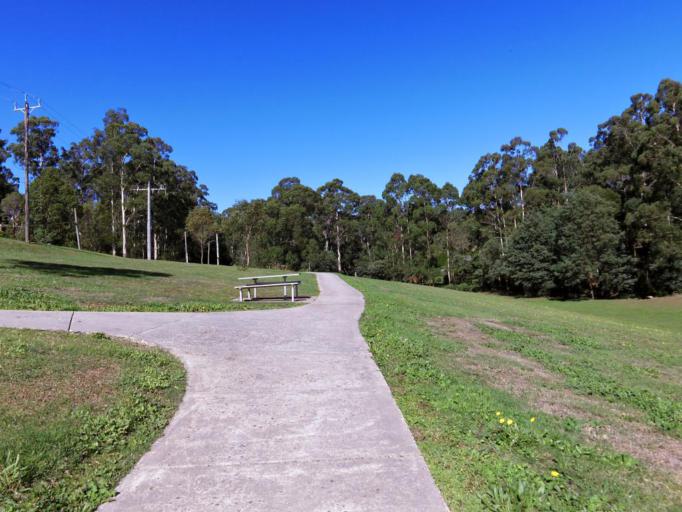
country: AU
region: Victoria
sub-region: Cardinia
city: Cockatoo
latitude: -37.9396
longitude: 145.4923
